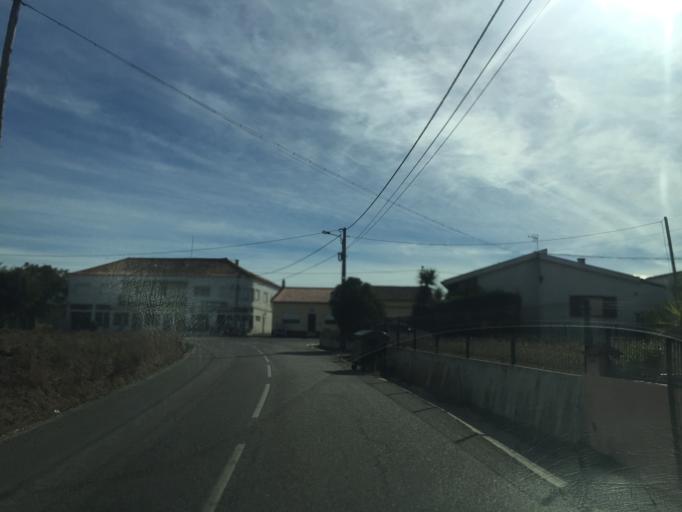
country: PT
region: Coimbra
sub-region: Figueira da Foz
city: Lavos
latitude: 40.0886
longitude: -8.8396
